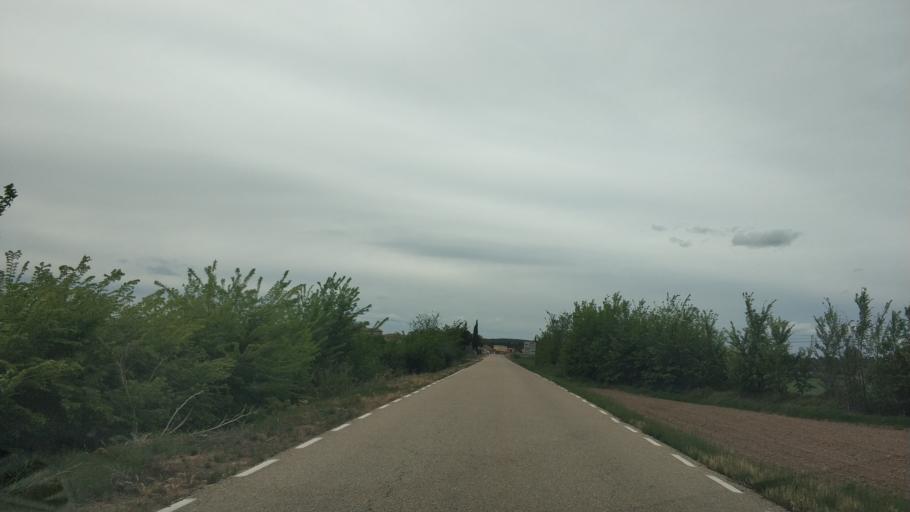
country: ES
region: Castille and Leon
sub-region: Provincia de Soria
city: Berlanga de Duero
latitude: 41.4921
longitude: -2.8680
